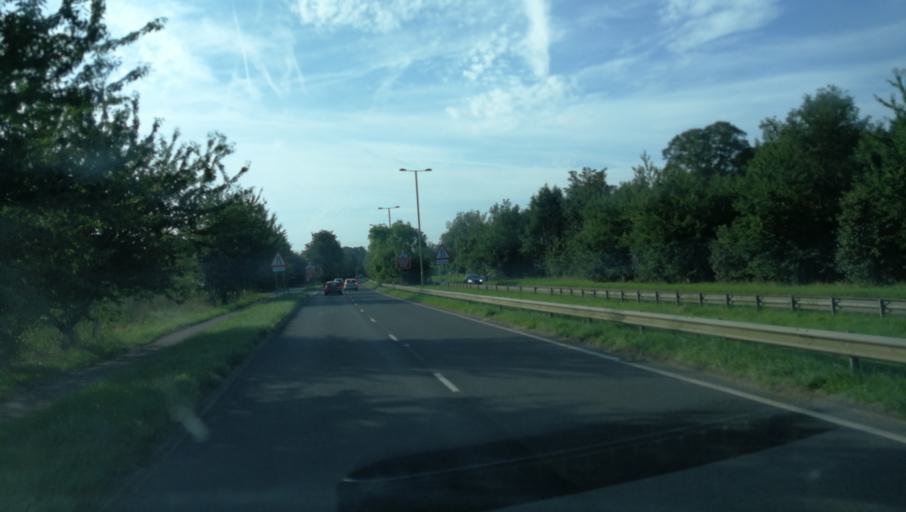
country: GB
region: England
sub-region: Oxfordshire
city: Yarnton
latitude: 51.8267
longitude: -1.3209
